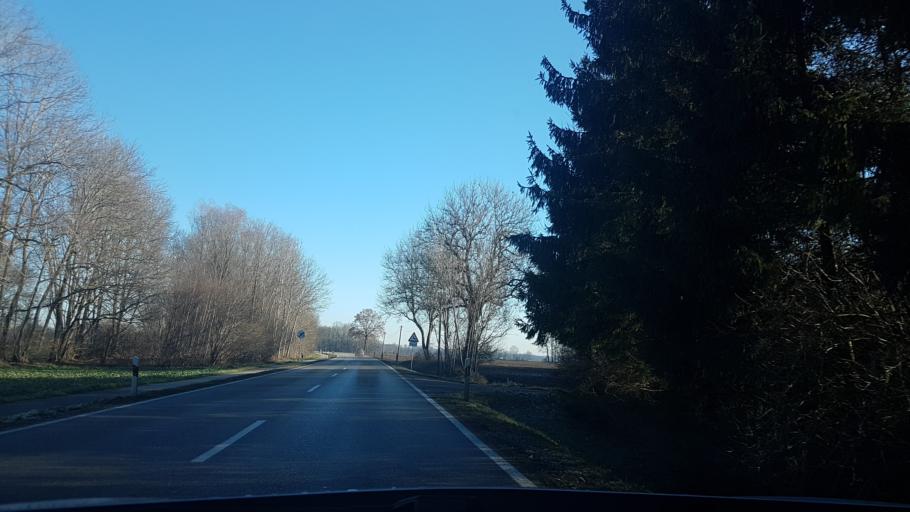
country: DE
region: Bavaria
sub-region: Upper Bavaria
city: Eichenried
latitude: 48.3110
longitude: 11.8005
